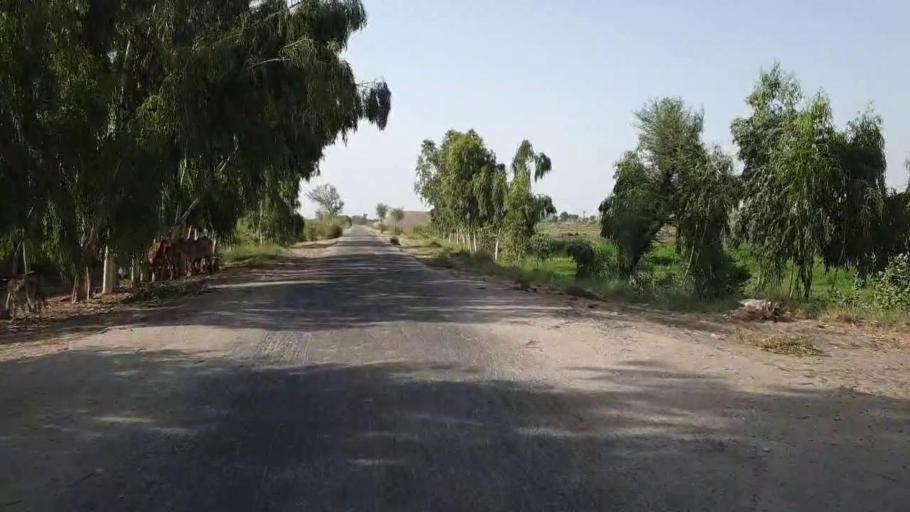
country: PK
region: Sindh
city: Kandiari
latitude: 26.6989
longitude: 68.9646
